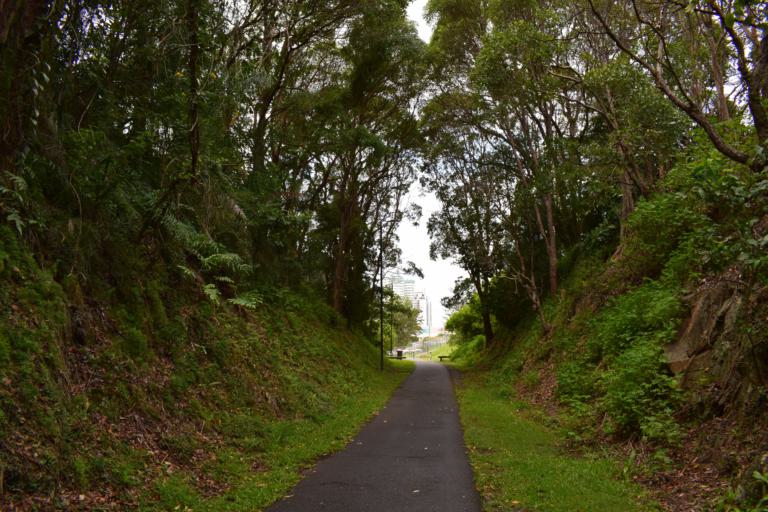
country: AU
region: New South Wales
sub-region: Tweed
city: Tweed Heads West
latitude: -28.1696
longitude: 153.5328
